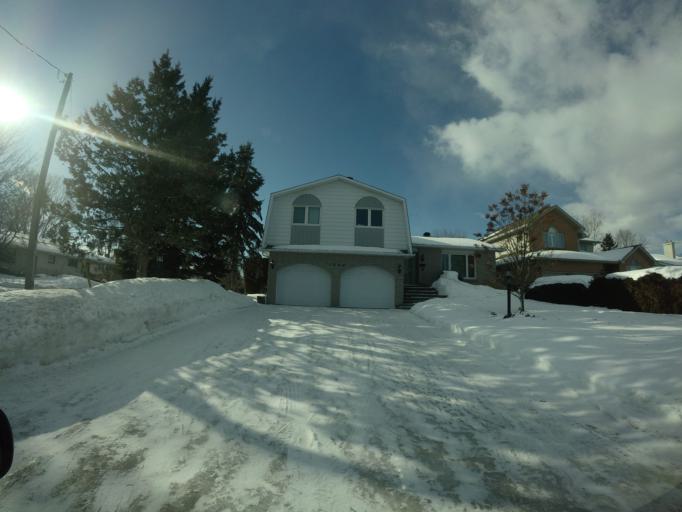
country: CA
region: Ontario
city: Ottawa
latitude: 45.4214
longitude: -75.6074
